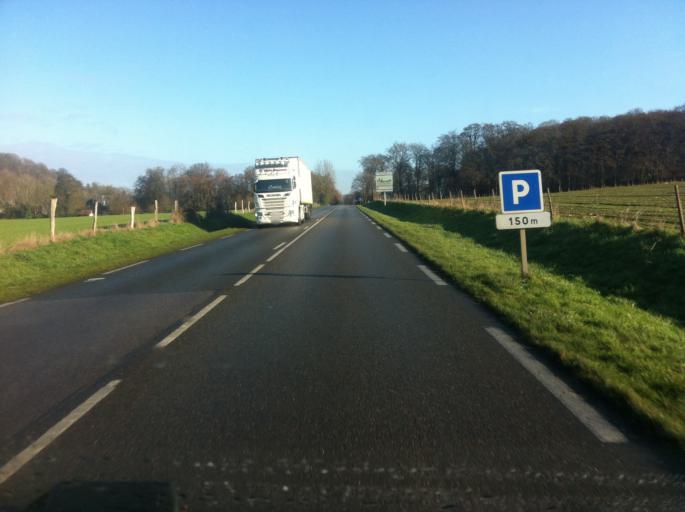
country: FR
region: Haute-Normandie
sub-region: Departement de la Seine-Maritime
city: Yainville
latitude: 49.4646
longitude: 0.8481
